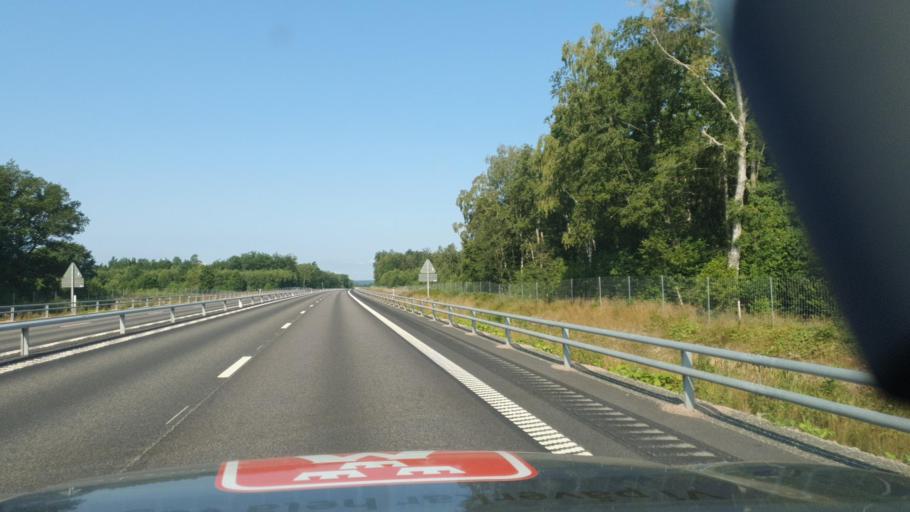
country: SE
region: Skane
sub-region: Kristianstads Kommun
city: Onnestad
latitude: 55.9611
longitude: 13.9832
